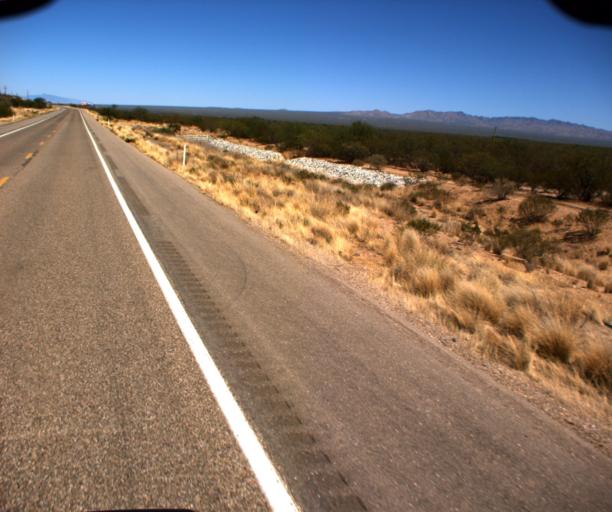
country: US
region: Arizona
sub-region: Pima County
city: Three Points
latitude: 32.0414
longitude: -111.4497
